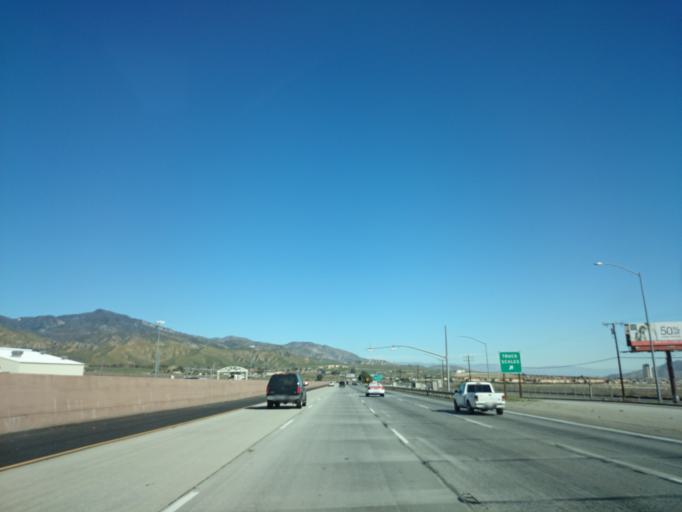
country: US
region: California
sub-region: Riverside County
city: Banning
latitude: 33.9295
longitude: -116.8393
